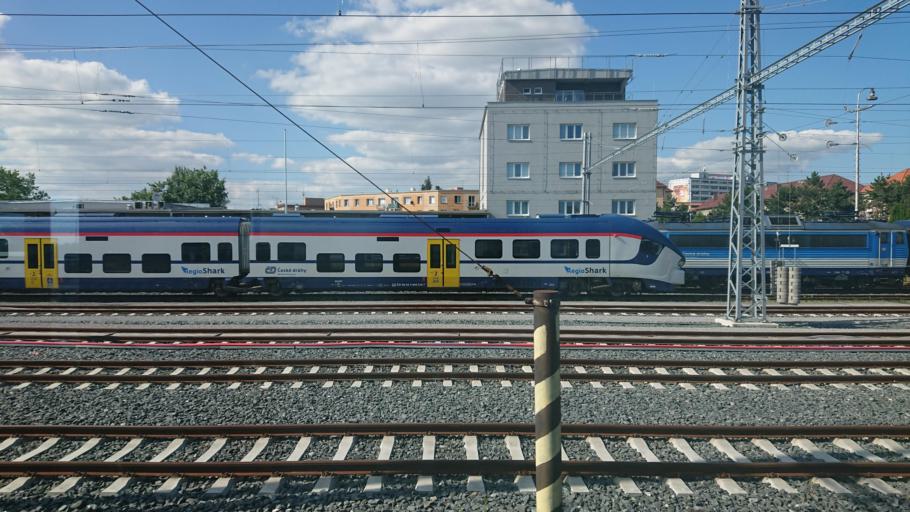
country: CZ
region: Pardubicky
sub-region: Okres Pardubice
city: Pardubice
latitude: 50.0317
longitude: 15.7629
